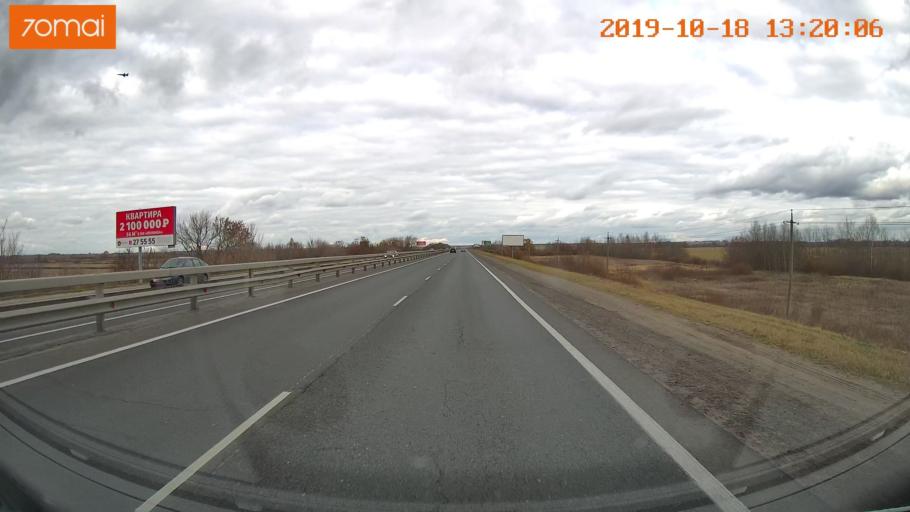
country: RU
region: Rjazan
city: Polyany
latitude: 54.6762
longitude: 39.8294
